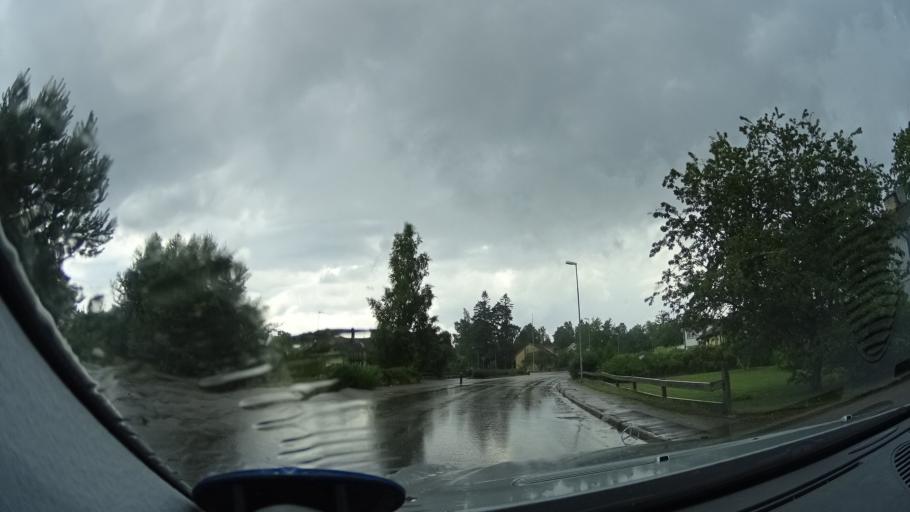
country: SE
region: Kalmar
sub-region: Emmaboda Kommun
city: Emmaboda
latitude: 56.6175
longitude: 15.5669
